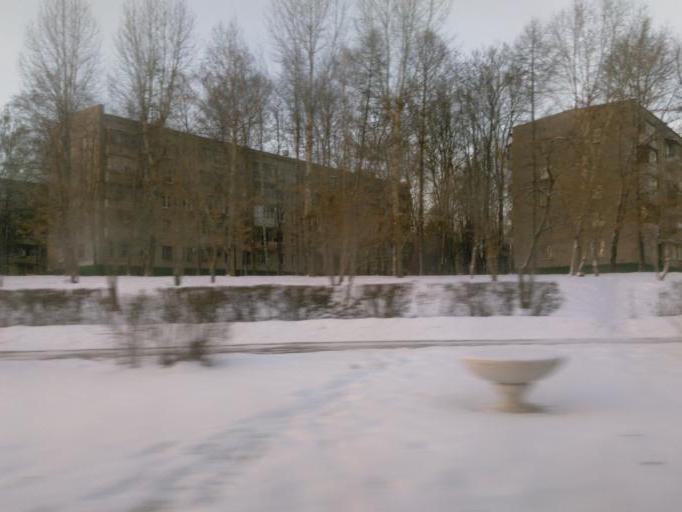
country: RU
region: Moscow
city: Solntsevo
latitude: 55.6532
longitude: 37.3890
